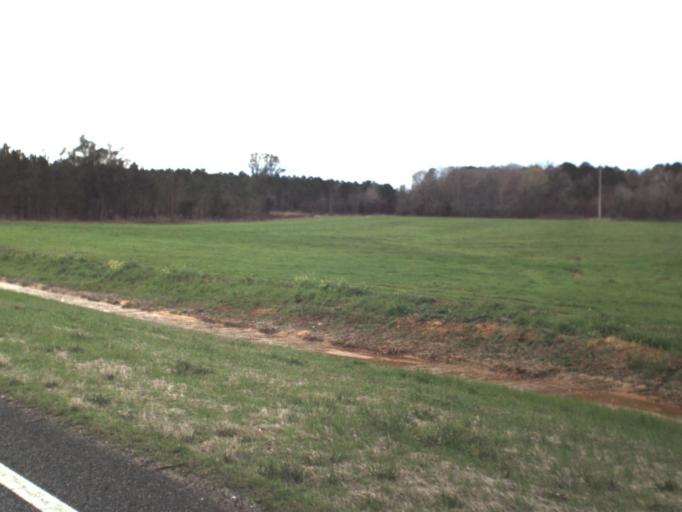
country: US
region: Florida
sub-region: Jackson County
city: Marianna
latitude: 30.8369
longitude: -85.3506
